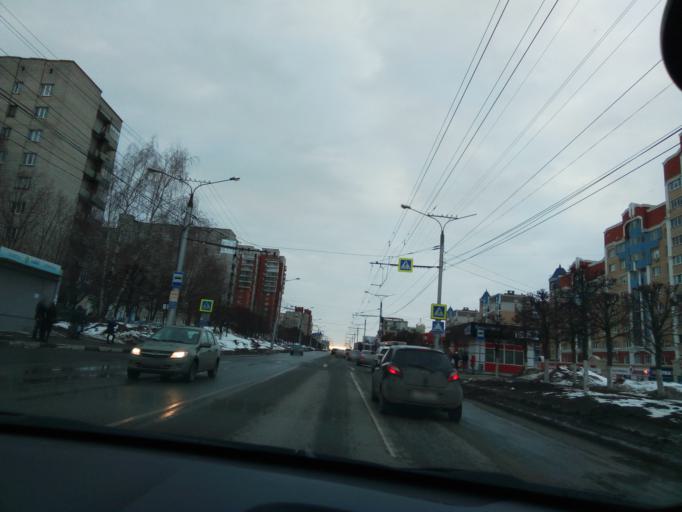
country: RU
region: Chuvashia
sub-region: Cheboksarskiy Rayon
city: Cheboksary
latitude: 56.1490
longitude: 47.1955
